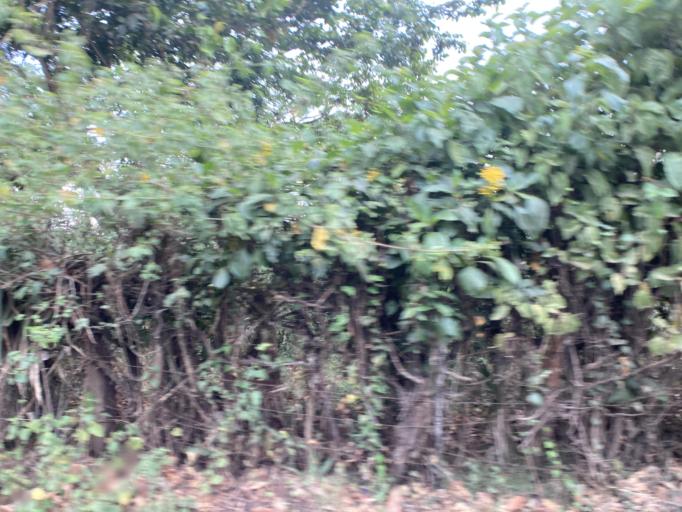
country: GT
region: Guatemala
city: Villa Canales
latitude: 14.4219
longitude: -90.5259
